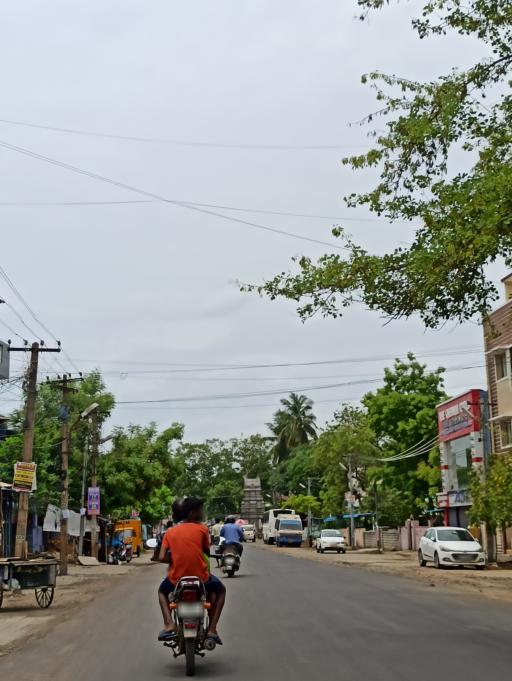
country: IN
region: Tamil Nadu
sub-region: Kancheepuram
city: Vandalur
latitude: 12.9274
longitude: 80.1093
